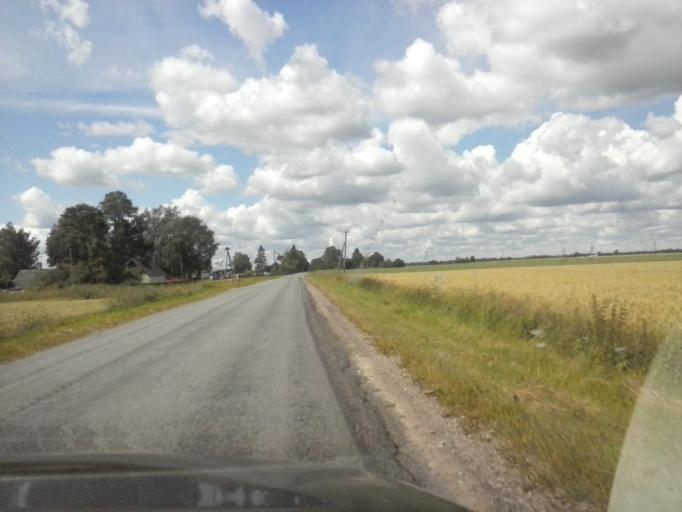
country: EE
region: Laeaene-Virumaa
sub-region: Rakke vald
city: Rakke
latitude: 59.0558
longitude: 26.3459
